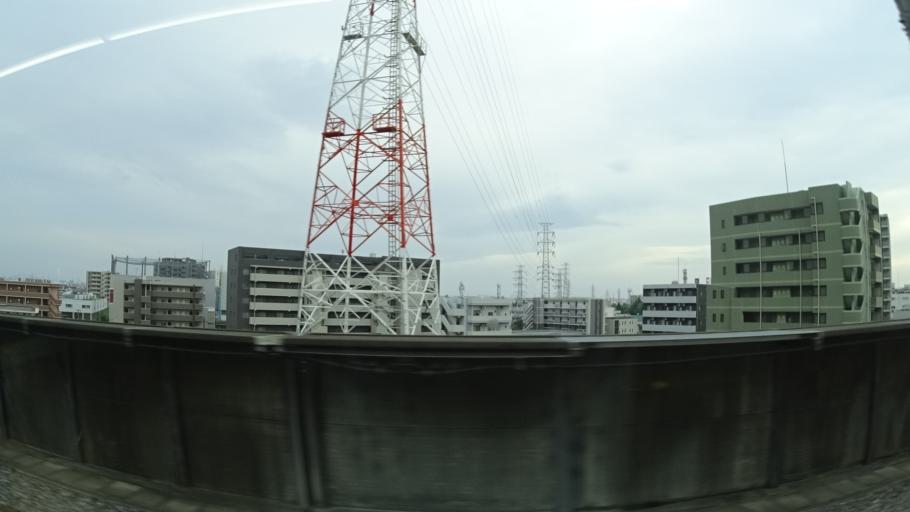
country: JP
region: Saitama
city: Shimotoda
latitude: 35.8270
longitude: 139.6608
